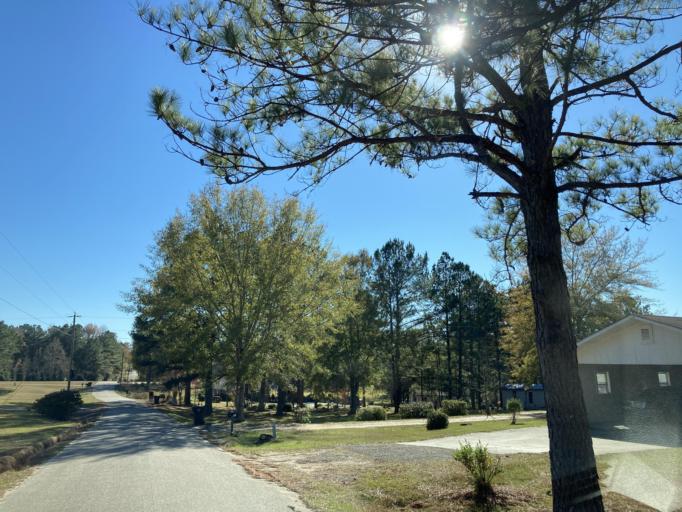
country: US
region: Mississippi
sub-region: Lamar County
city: Sumrall
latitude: 31.2911
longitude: -89.6457
